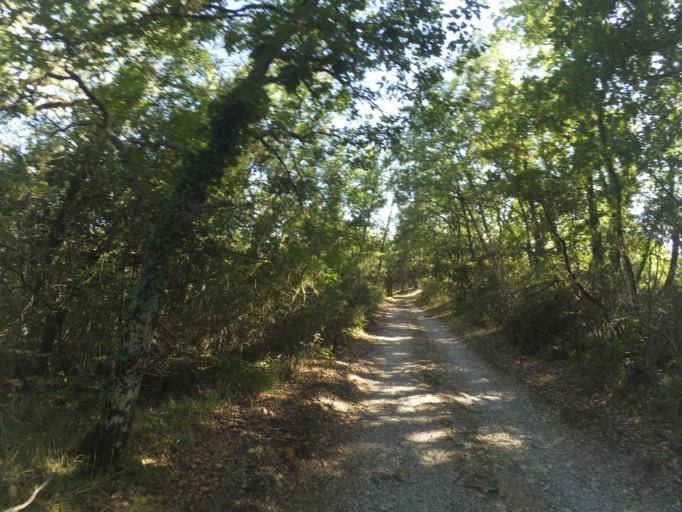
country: IT
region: Tuscany
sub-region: Province of Arezzo
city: Castiglion Fibocchi
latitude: 43.5434
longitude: 11.7674
